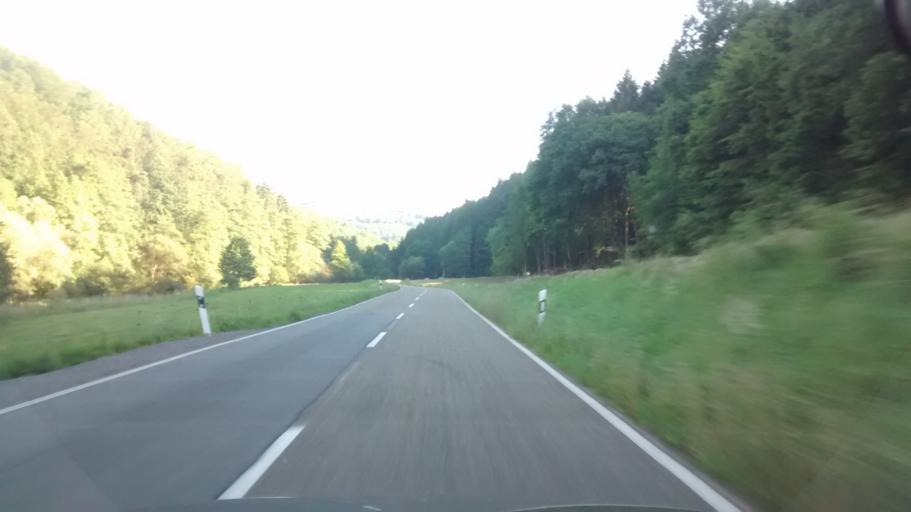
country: DE
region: Rheinland-Pfalz
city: Niederschlettenbach
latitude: 49.0992
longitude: 7.8495
